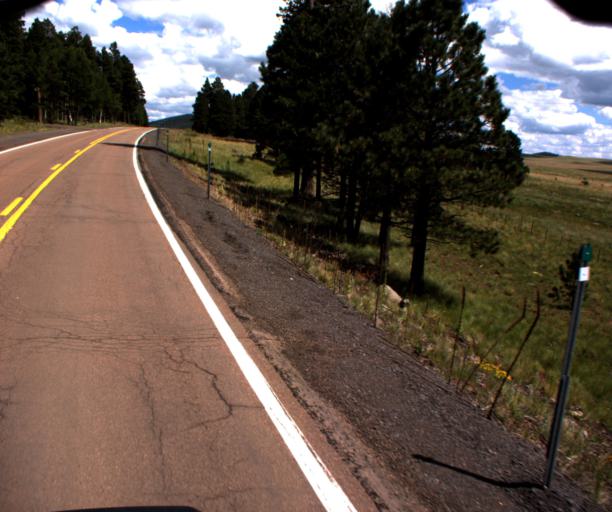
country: US
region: Arizona
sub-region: Apache County
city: Eagar
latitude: 34.0552
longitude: -109.5658
